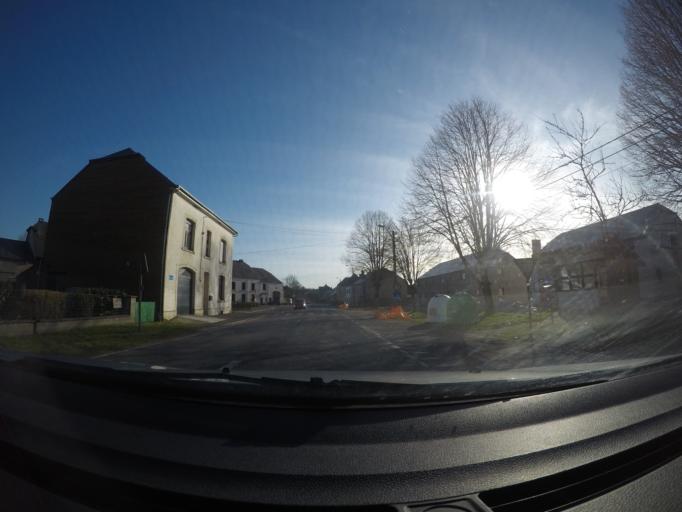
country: BE
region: Wallonia
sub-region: Province du Luxembourg
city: Tintigny
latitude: 49.6911
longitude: 5.5230
